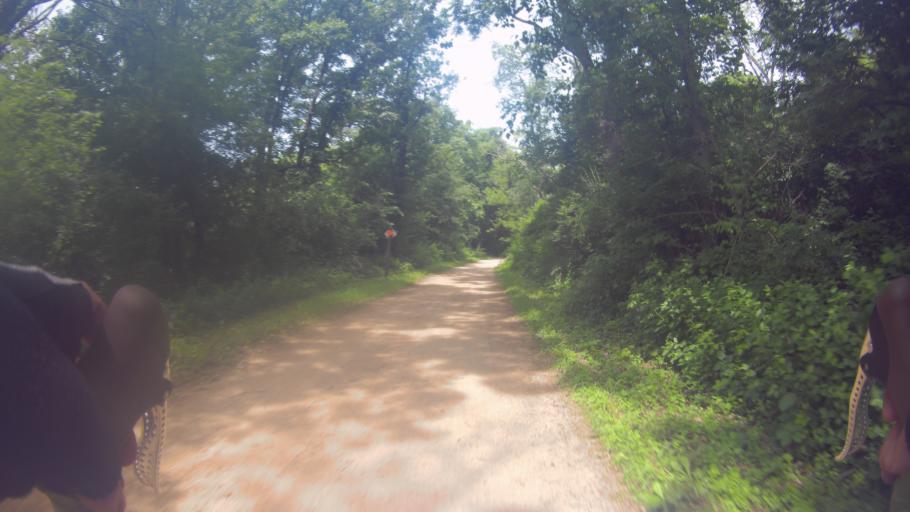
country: US
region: Wisconsin
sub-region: Dane County
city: Mount Horeb
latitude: 43.0149
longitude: -89.7030
